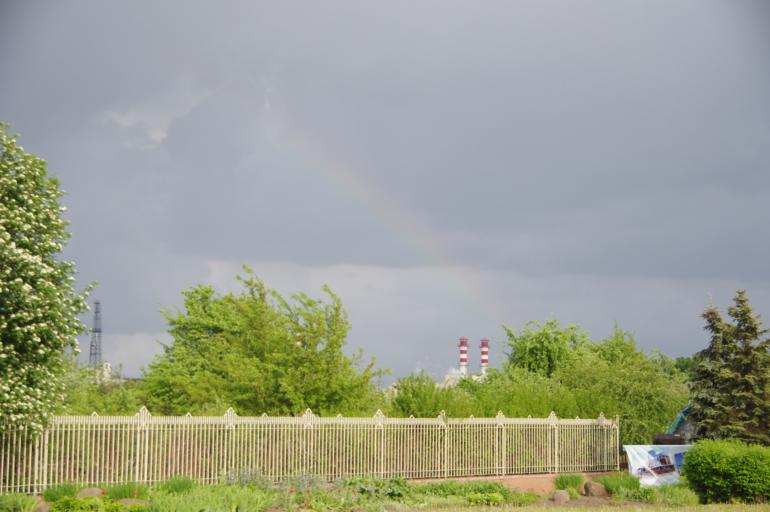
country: BY
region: Minsk
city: Minsk
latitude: 53.8854
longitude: 27.5675
